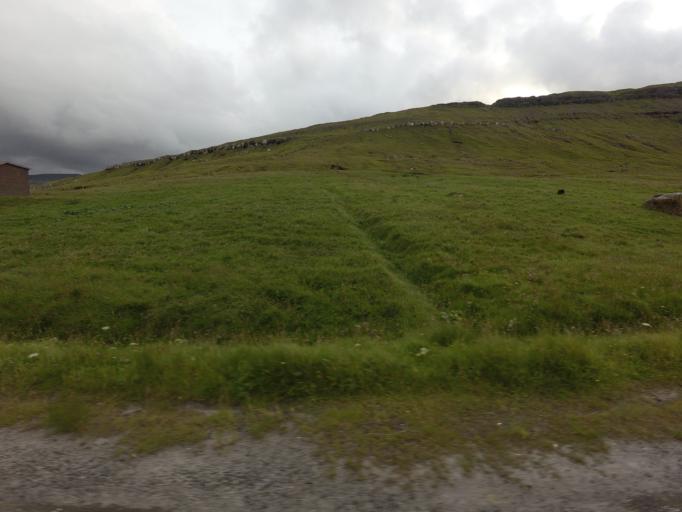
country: FO
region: Streymoy
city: Kollafjordhur
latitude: 62.1300
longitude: -6.8798
